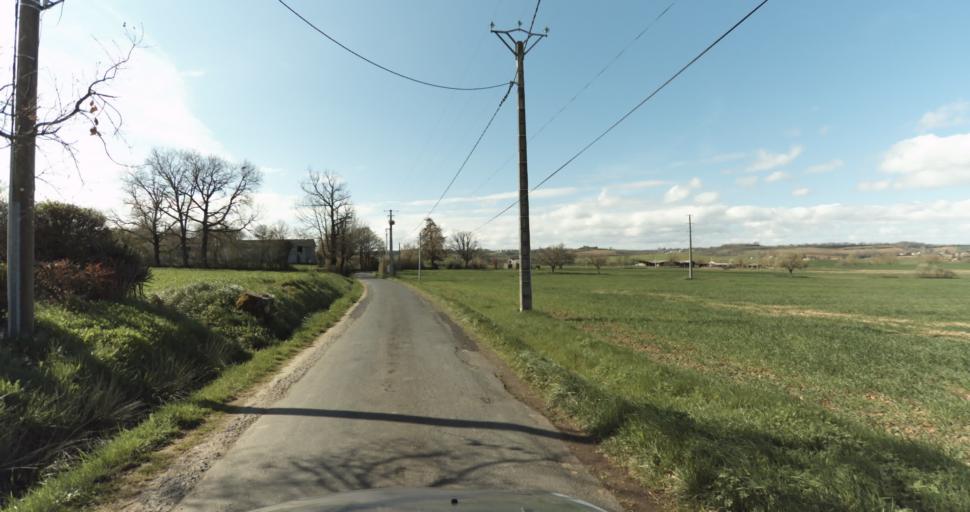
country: FR
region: Midi-Pyrenees
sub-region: Departement du Tarn
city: Puygouzon
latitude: 43.8886
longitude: 2.1850
